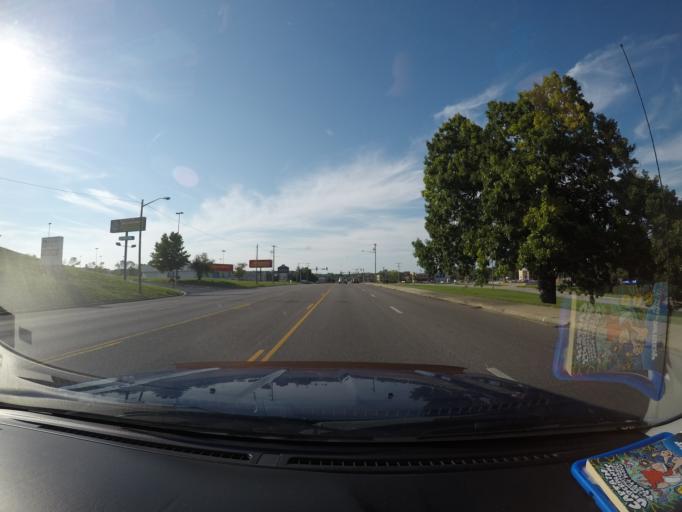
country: US
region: Kansas
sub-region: Leavenworth County
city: Leavenworth
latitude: 39.2839
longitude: -94.9035
